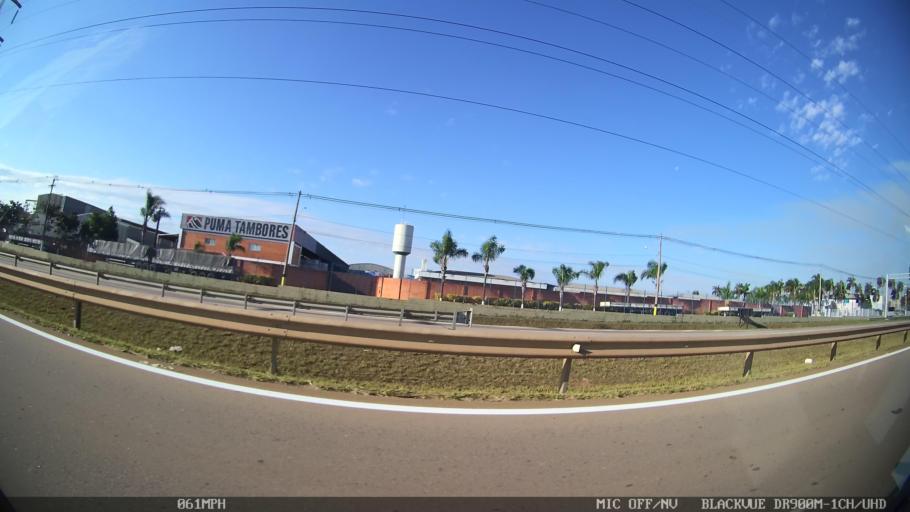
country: BR
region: Sao Paulo
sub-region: Piracicaba
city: Piracicaba
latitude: -22.6663
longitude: -47.6060
